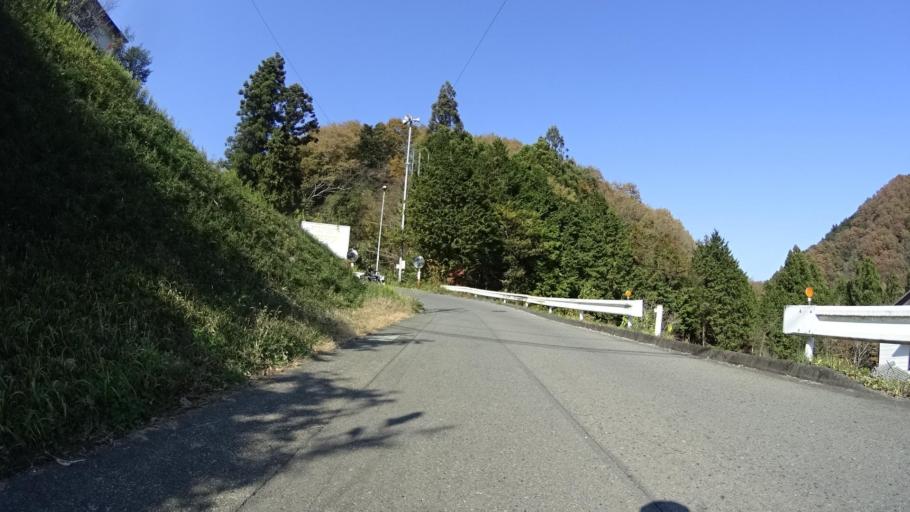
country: JP
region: Yamanashi
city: Uenohara
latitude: 35.5833
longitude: 139.1546
